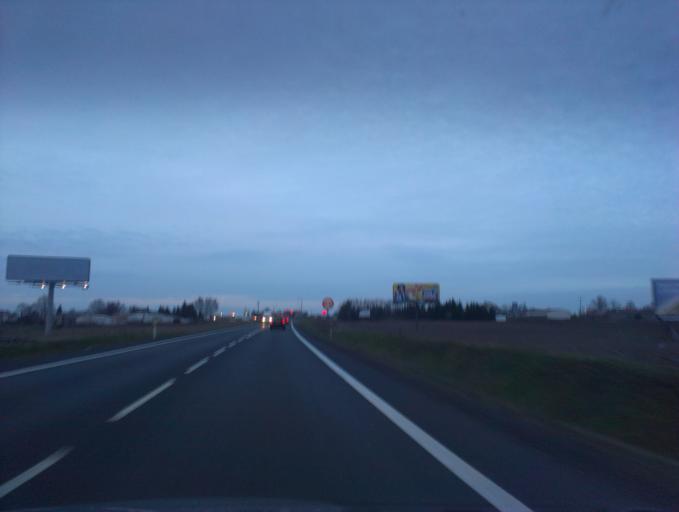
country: PL
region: Greater Poland Voivodeship
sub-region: Powiat poznanski
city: Zlotniki
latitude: 52.5566
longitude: 16.8351
